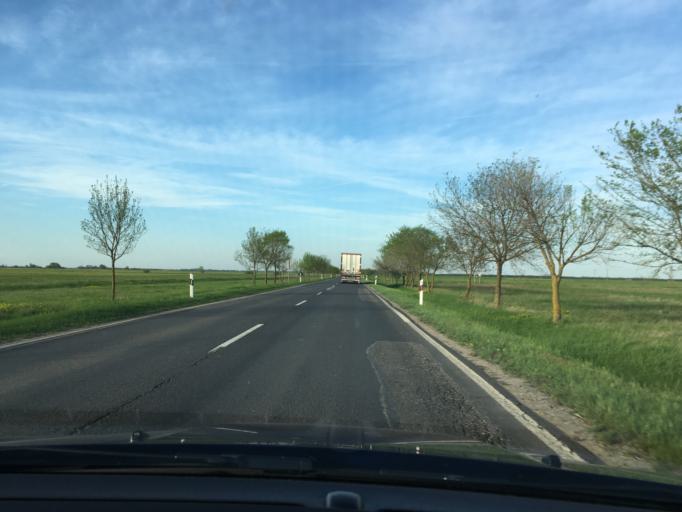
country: HU
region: Hajdu-Bihar
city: Berettyoujfalu
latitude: 47.1512
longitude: 21.4954
